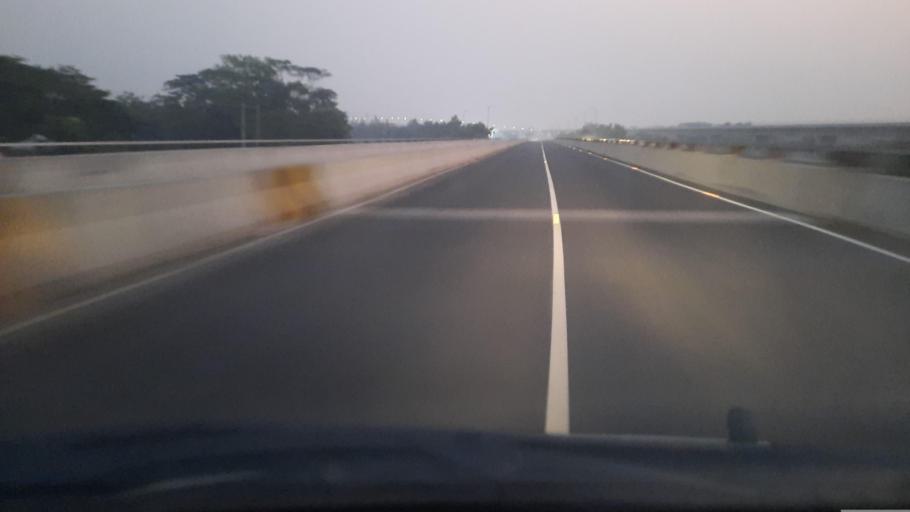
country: BD
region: Dhaka
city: Char Bhadrasan
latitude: 23.4029
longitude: 90.2489
